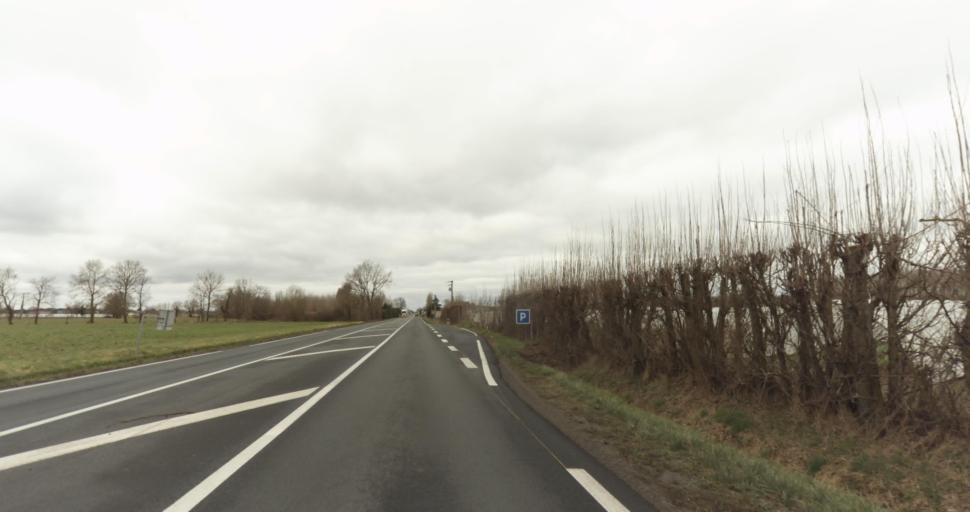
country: FR
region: Pays de la Loire
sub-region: Departement de Maine-et-Loire
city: Vivy
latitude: 47.3166
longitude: -0.0470
